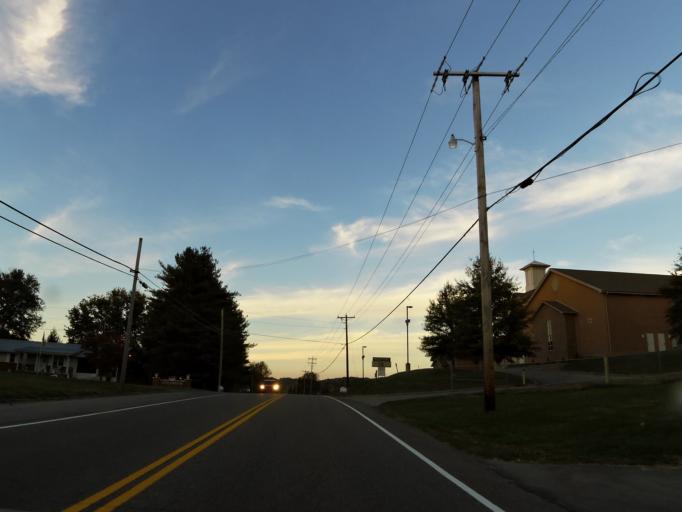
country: US
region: Tennessee
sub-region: Blount County
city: Eagleton Village
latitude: 35.8373
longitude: -83.9417
